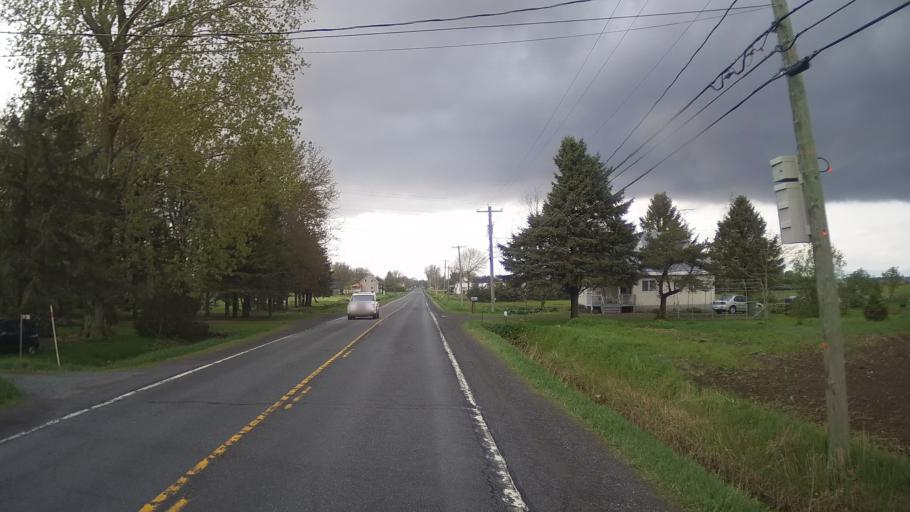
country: CA
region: Quebec
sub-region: Monteregie
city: Rougemont
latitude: 45.3410
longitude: -73.0907
